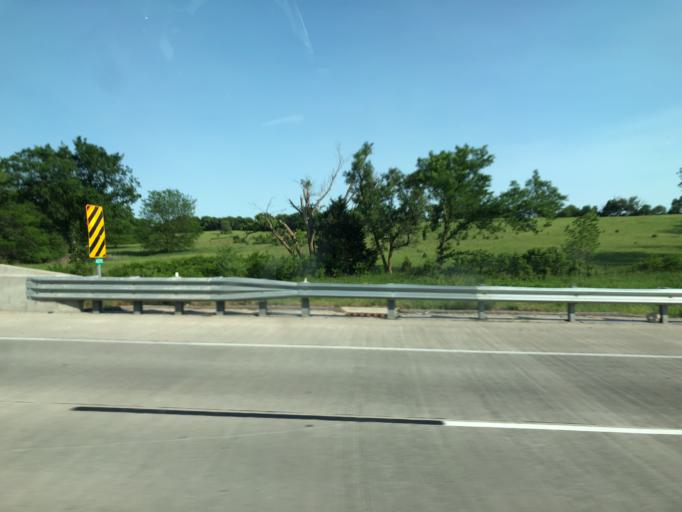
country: US
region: Nebraska
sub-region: Saunders County
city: Ashland
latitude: 40.9887
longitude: -96.3644
